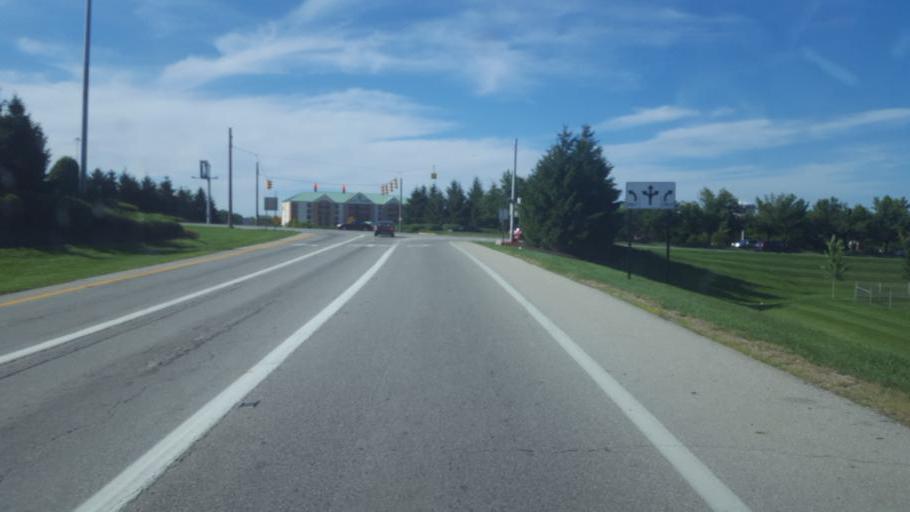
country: US
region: Ohio
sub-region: Franklin County
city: Dublin
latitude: 40.0751
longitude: -83.1342
